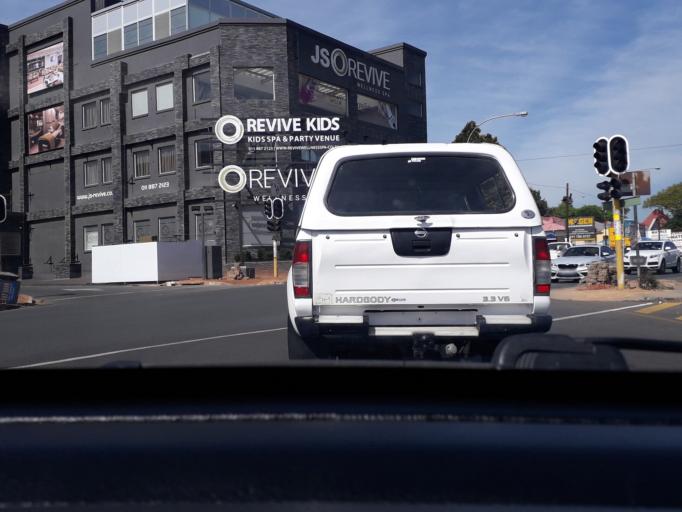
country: ZA
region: Gauteng
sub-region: City of Johannesburg Metropolitan Municipality
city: Johannesburg
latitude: -26.1387
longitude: 28.0899
